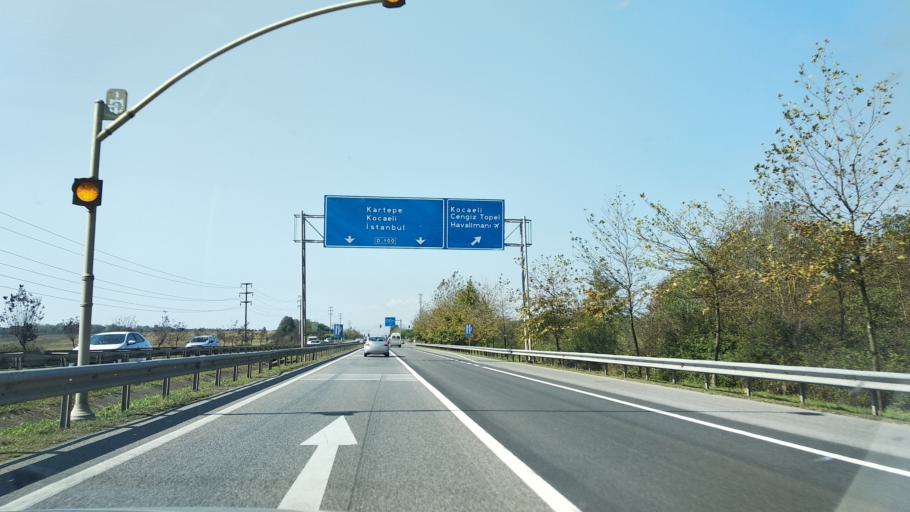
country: TR
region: Kocaeli
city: Derbent
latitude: 40.7428
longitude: 30.0842
